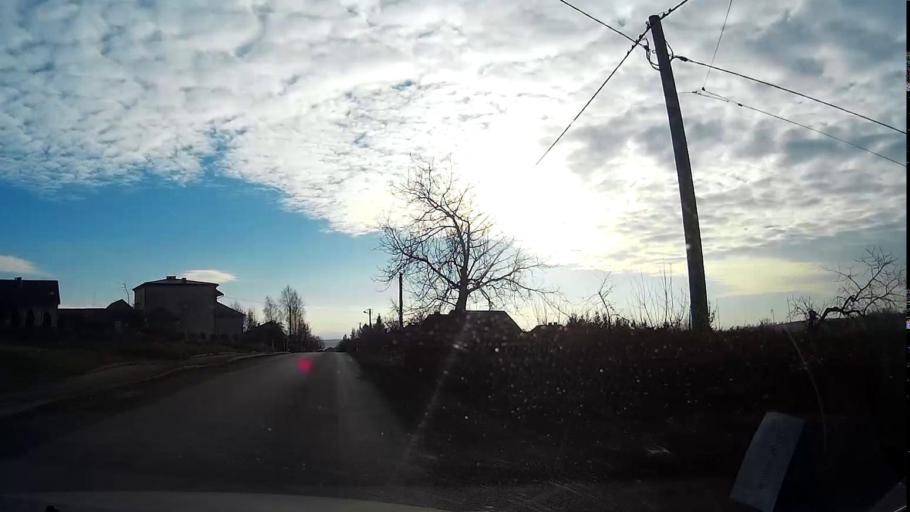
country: PL
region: Lesser Poland Voivodeship
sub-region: Powiat krakowski
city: Sanka
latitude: 50.0637
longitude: 19.6580
